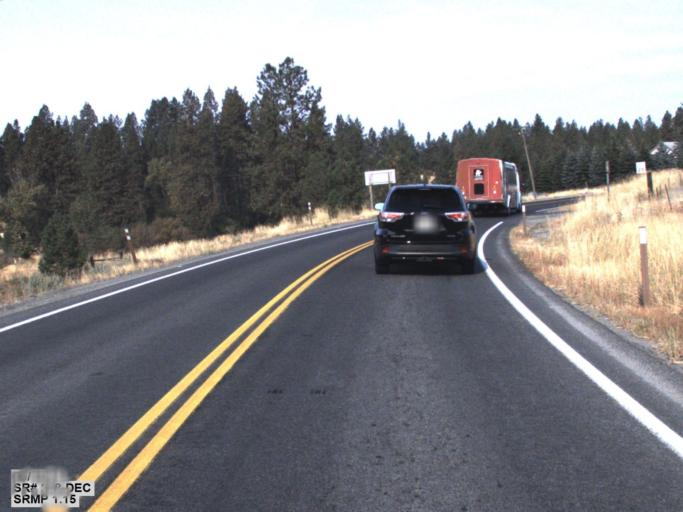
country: US
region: Washington
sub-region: Spokane County
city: Veradale
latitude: 47.4443
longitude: -117.1251
